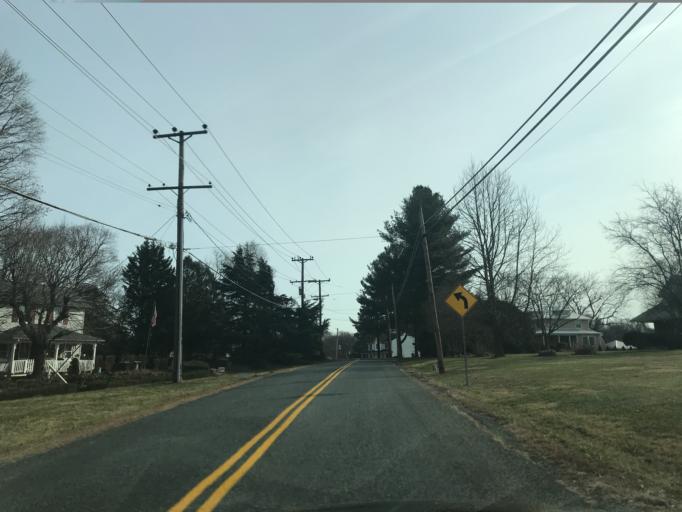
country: US
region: Maryland
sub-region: Harford County
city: Aberdeen
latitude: 39.5726
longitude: -76.1647
